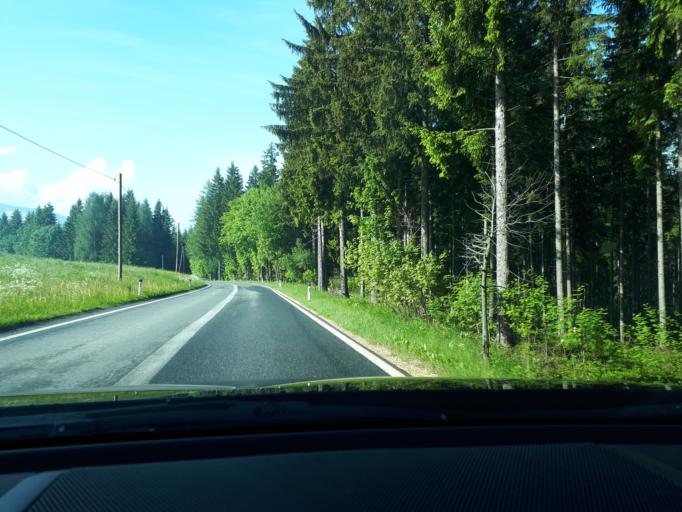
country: AT
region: Carinthia
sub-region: Politischer Bezirk Wolfsberg
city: Preitenegg
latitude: 46.9386
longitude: 14.9643
